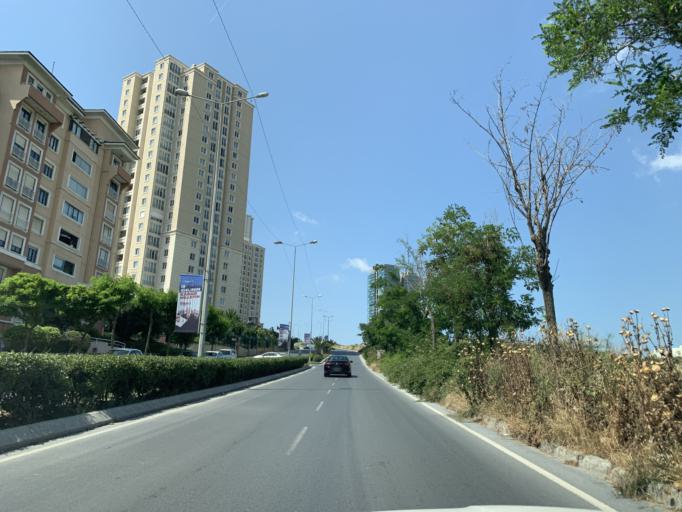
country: TR
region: Istanbul
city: Esenyurt
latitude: 41.0702
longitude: 28.7002
